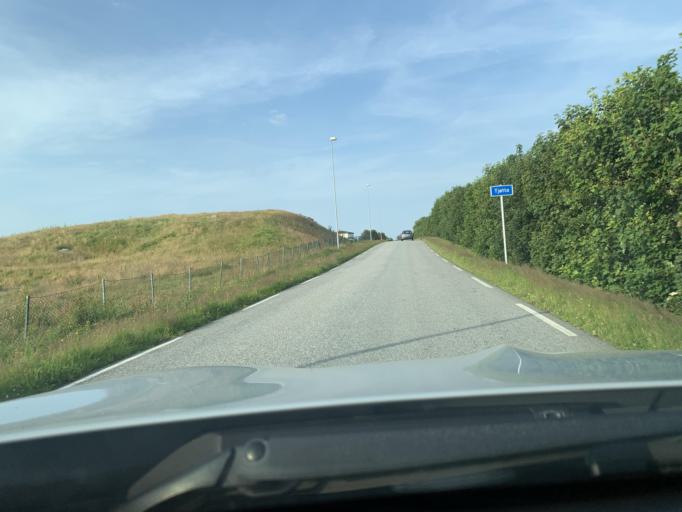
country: NO
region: Rogaland
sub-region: Time
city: Bryne
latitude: 58.7362
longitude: 5.6052
